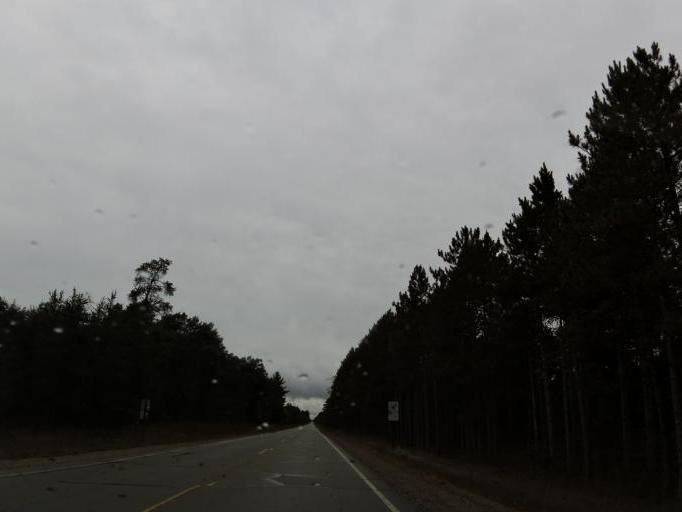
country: US
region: Michigan
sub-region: Roscommon County
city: Roscommon
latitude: 44.4639
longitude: -84.5338
